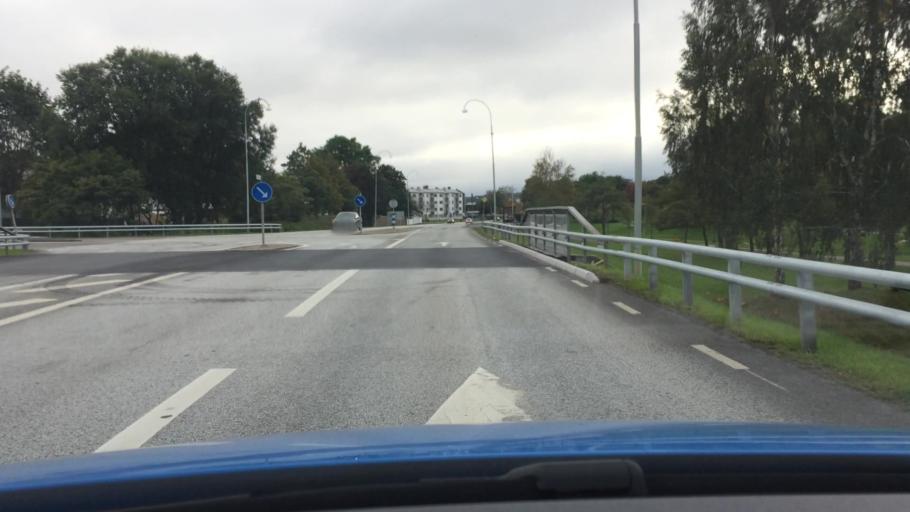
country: SE
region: Halland
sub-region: Kungsbacka Kommun
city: Kungsbacka
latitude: 57.4896
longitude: 12.0894
